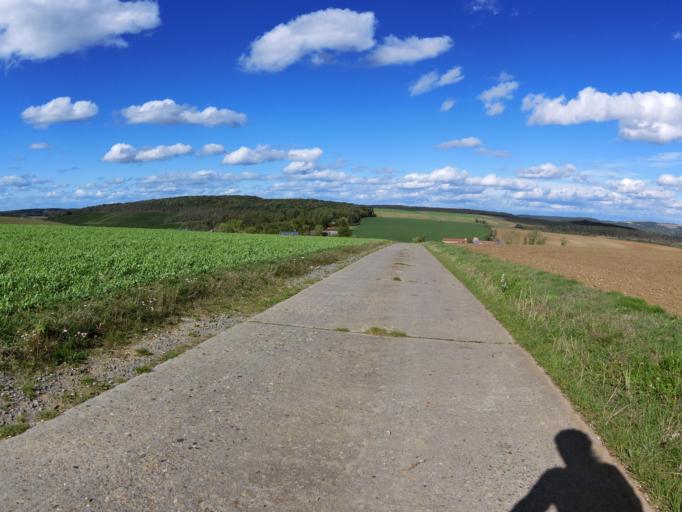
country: DE
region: Bavaria
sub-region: Regierungsbezirk Unterfranken
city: Erlabrunn
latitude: 49.8357
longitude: 9.8294
